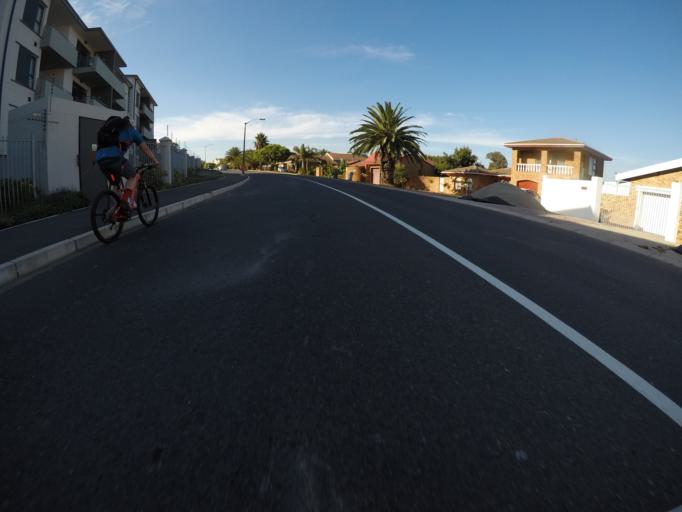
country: ZA
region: Western Cape
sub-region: City of Cape Town
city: Kraaifontein
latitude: -33.8778
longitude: 18.6457
